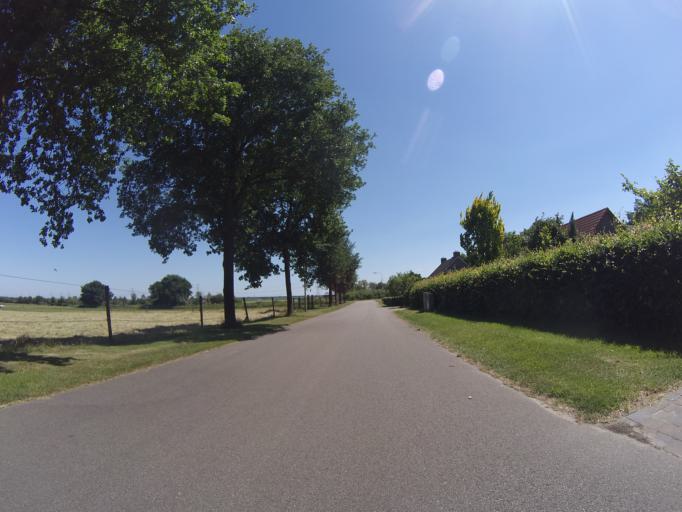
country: NL
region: Drenthe
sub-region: Gemeente Emmen
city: Emmen
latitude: 52.8202
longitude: 6.9245
